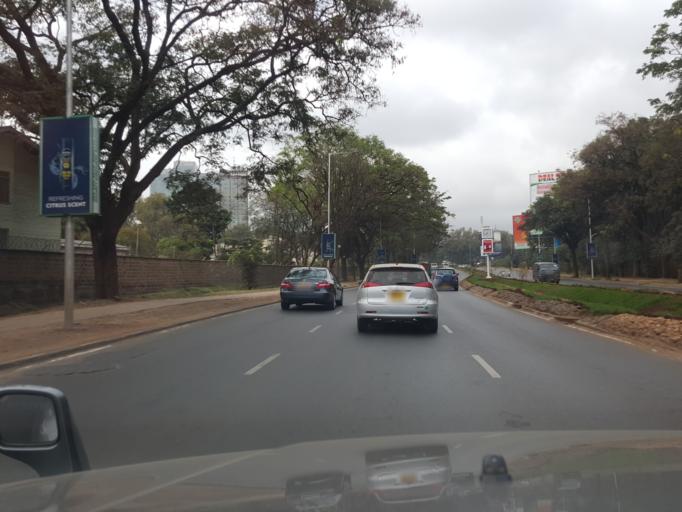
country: KE
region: Nairobi Area
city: Nairobi
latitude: -1.2773
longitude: 36.8138
